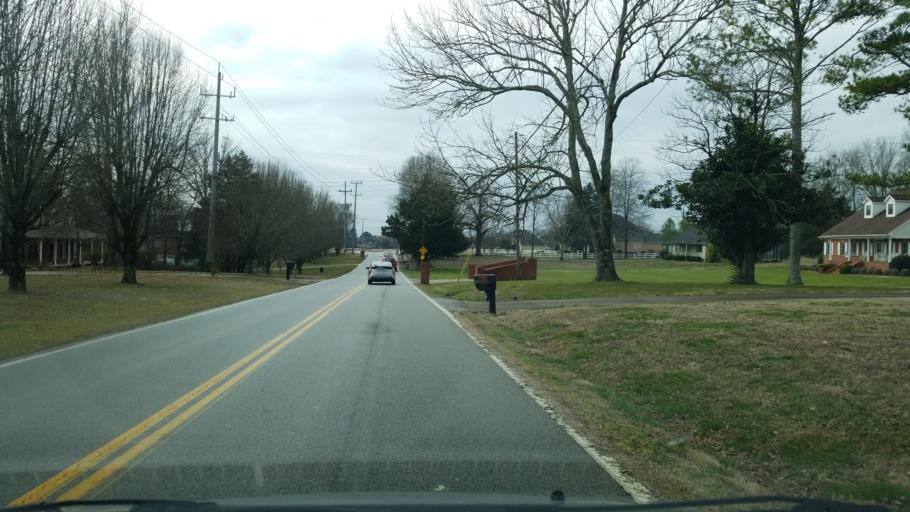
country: US
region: Tennessee
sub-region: Hamilton County
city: Collegedale
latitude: 35.0161
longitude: -85.0891
